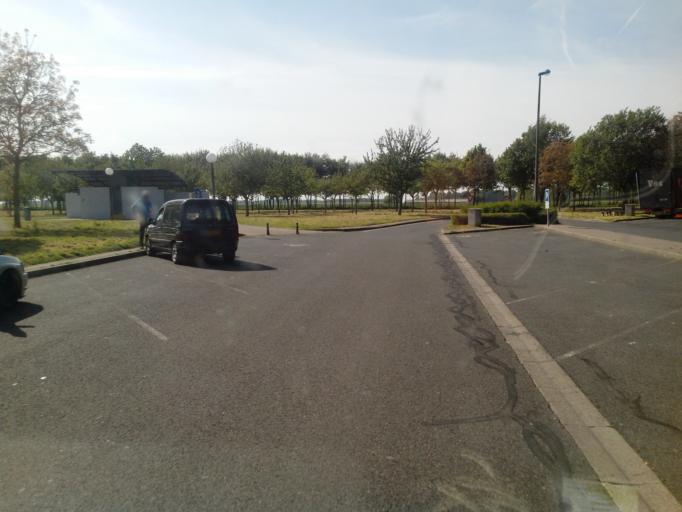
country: FR
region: Picardie
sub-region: Departement de la Somme
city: Oisemont
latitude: 50.0452
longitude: 1.7602
